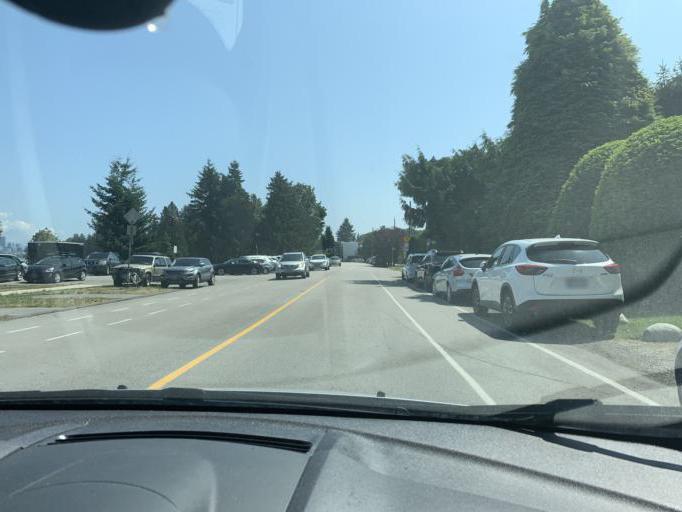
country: CA
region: British Columbia
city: West End
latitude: 49.2751
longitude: -123.2122
